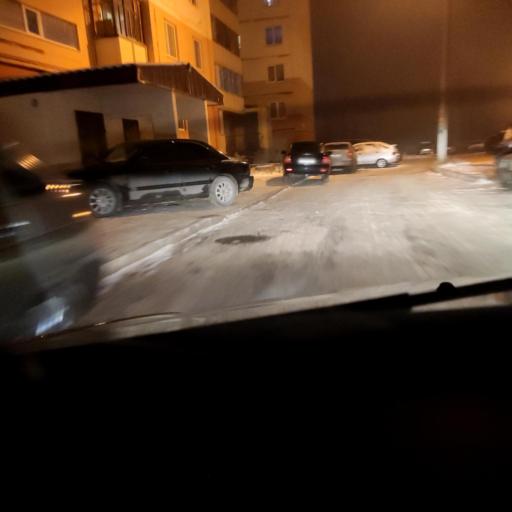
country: RU
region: Bashkortostan
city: Iglino
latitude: 54.7551
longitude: 56.2411
